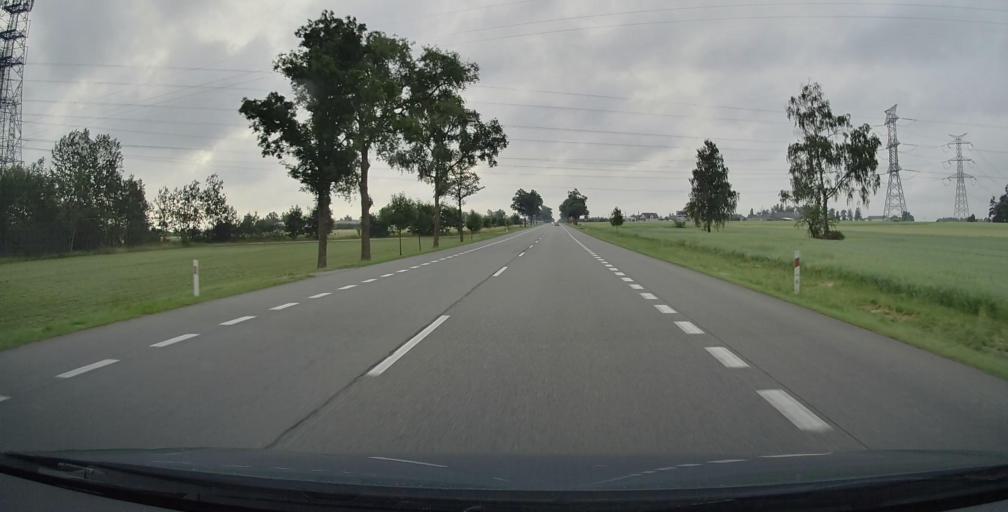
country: PL
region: Masovian Voivodeship
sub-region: Powiat siedlecki
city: Wisniew
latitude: 52.1208
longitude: 22.3564
